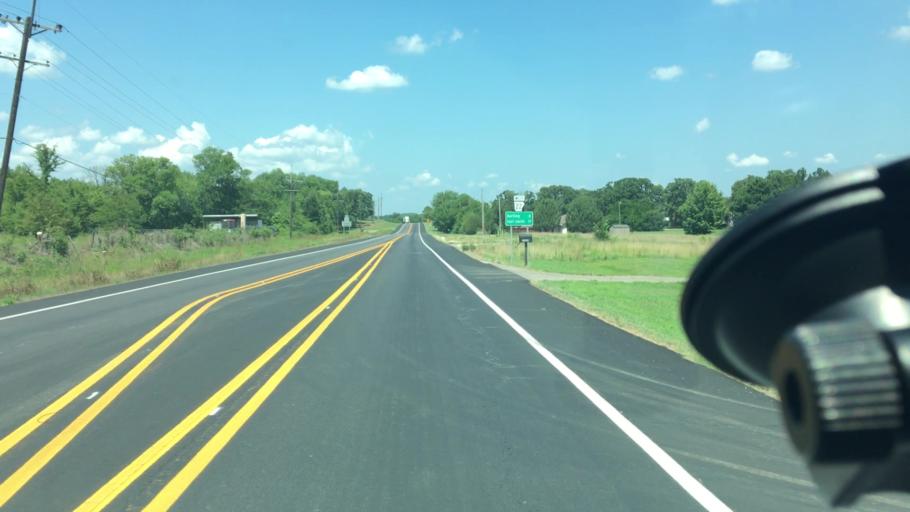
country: US
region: Arkansas
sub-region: Sebastian County
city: Lavaca
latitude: 35.3022
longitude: -94.1632
